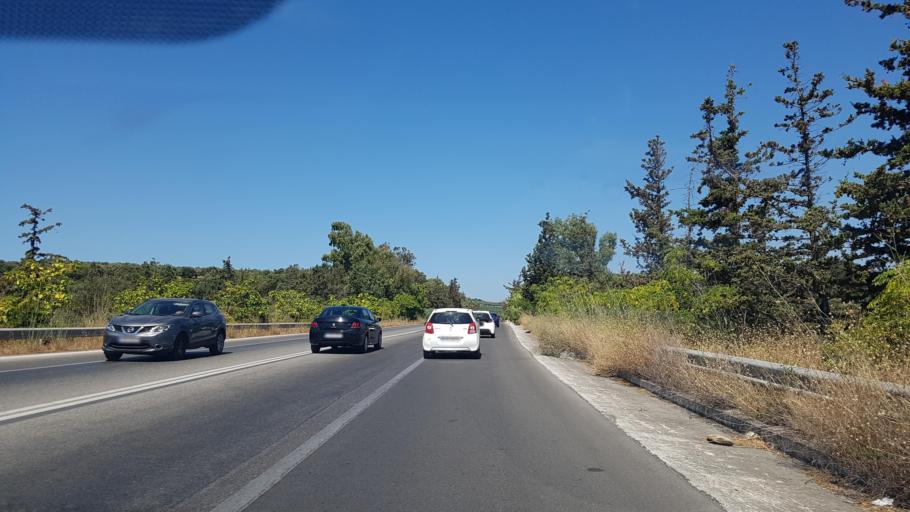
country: GR
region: Crete
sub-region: Nomos Chanias
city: Gerani
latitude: 35.5137
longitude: 23.8531
